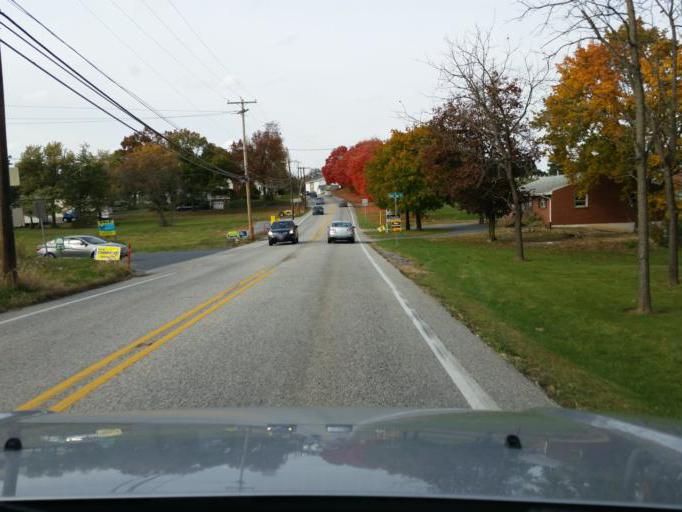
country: US
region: Pennsylvania
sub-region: Dauphin County
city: Skyline View
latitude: 40.3187
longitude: -76.7015
